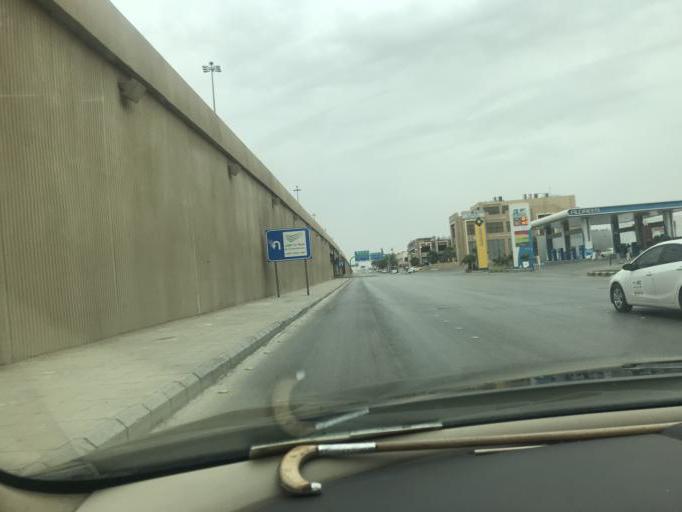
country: SA
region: Ar Riyad
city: Riyadh
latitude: 24.7913
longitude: 46.7010
